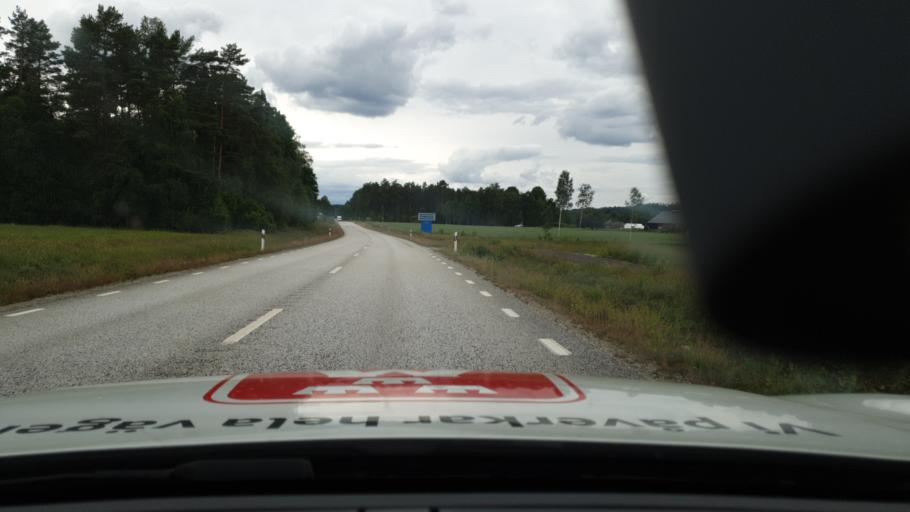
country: SE
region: Joenkoeping
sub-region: Gnosjo Kommun
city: Hillerstorp
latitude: 57.2875
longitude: 13.8293
